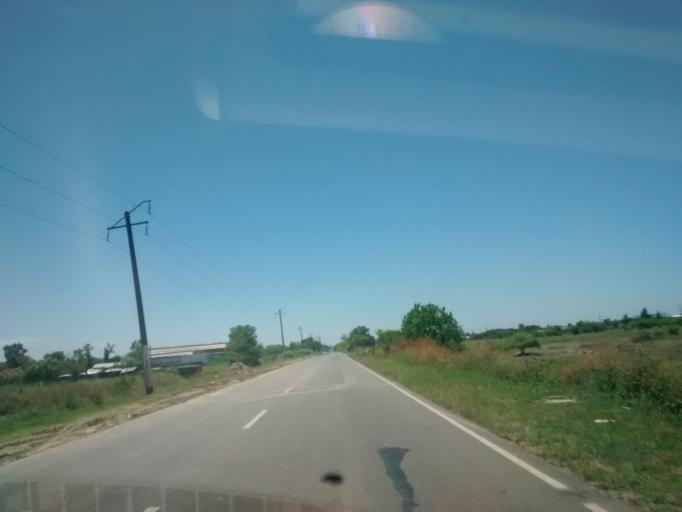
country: AR
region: Buenos Aires
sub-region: Partido de Berisso
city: Berisso
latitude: -34.8877
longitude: -57.8638
